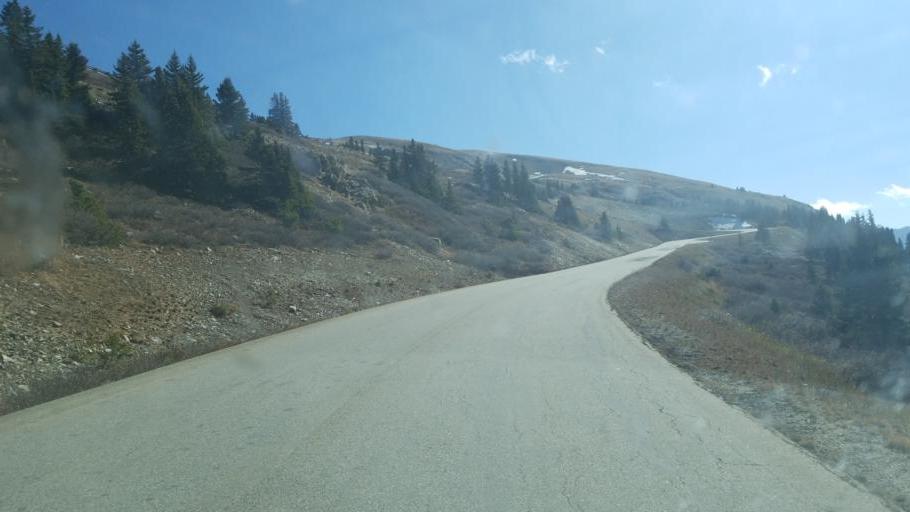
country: US
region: Colorado
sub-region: Chaffee County
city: Buena Vista
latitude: 38.8267
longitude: -106.4064
